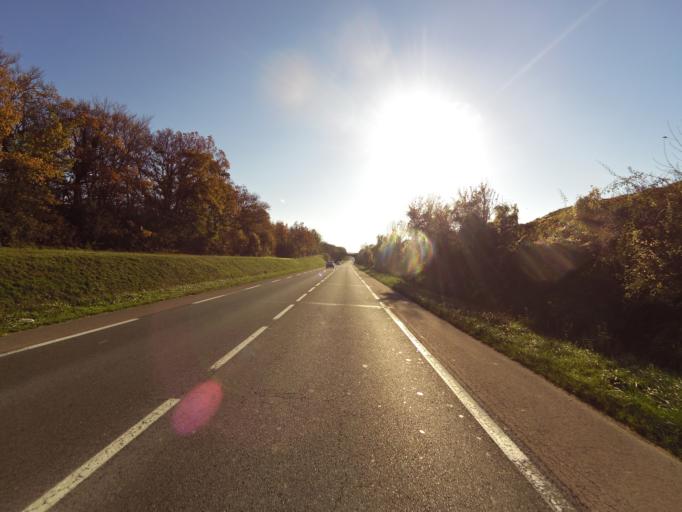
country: FR
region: Champagne-Ardenne
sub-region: Departement de l'Aube
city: Breviandes
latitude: 48.2549
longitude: 4.1046
